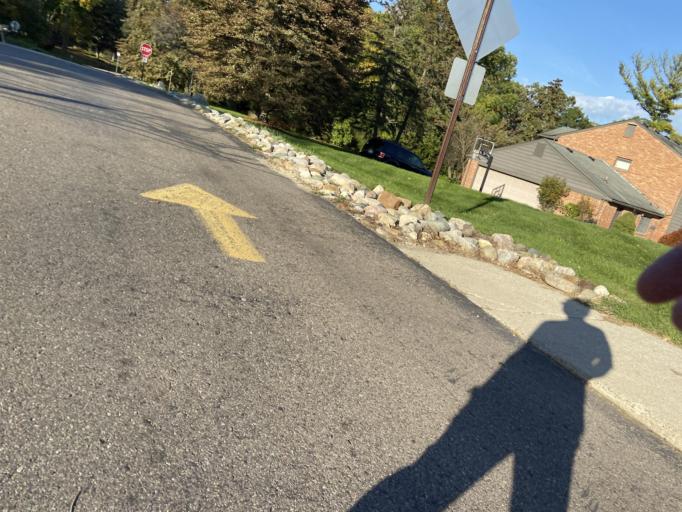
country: US
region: Michigan
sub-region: Oakland County
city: Franklin
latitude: 42.5051
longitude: -83.3288
